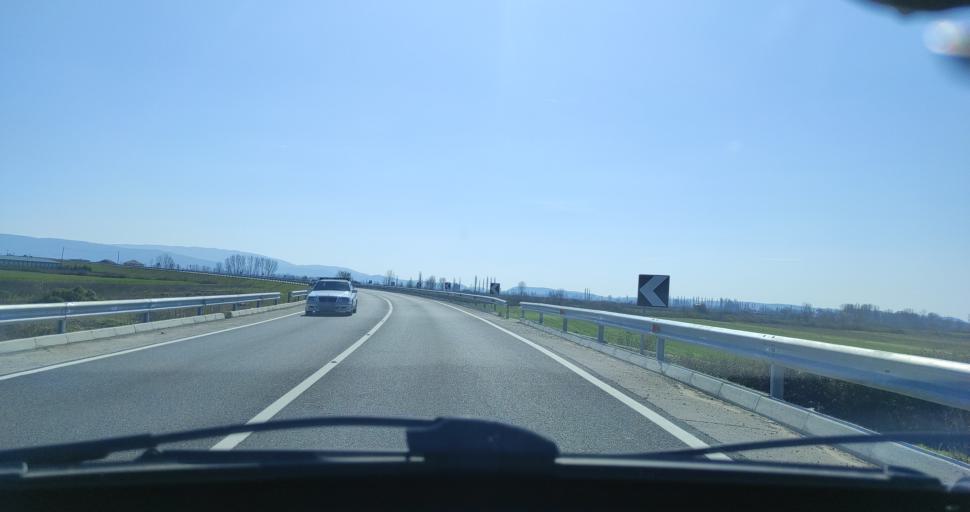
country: AL
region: Shkoder
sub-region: Rrethi i Shkodres
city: Berdica e Madhe
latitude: 42.0147
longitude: 19.4755
